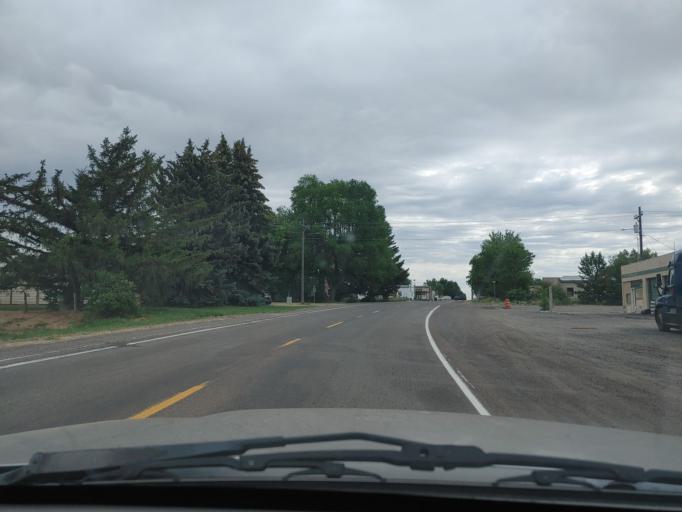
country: US
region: Idaho
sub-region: Lincoln County
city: Shoshone
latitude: 43.0492
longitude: -114.1562
